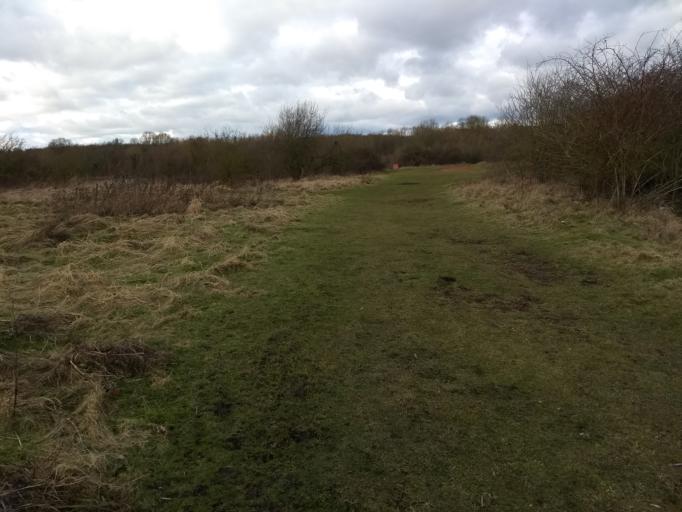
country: GB
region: England
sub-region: Buckinghamshire
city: Bletchley
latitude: 51.9865
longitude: -0.7354
